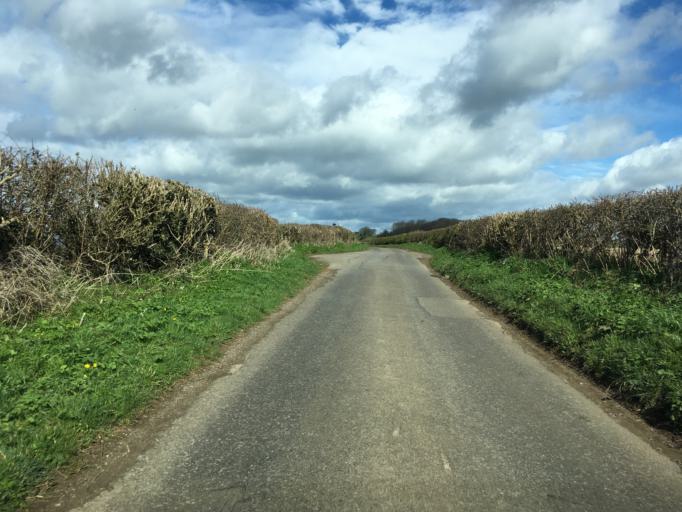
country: GB
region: England
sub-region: South Gloucestershire
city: Horton
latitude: 51.5501
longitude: -2.3408
